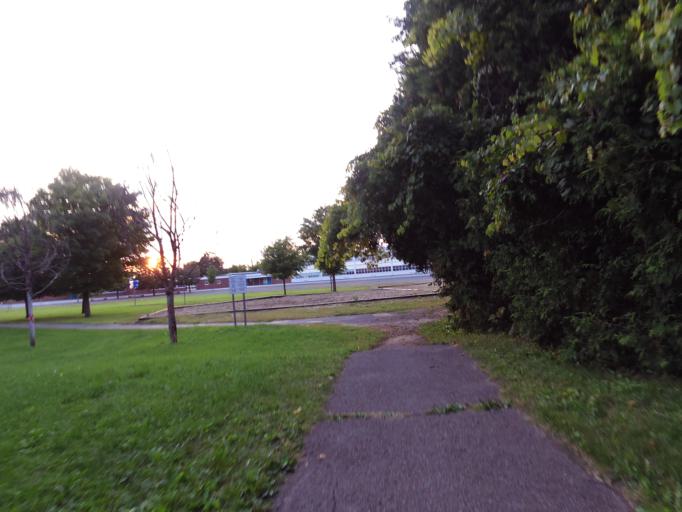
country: CA
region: Ontario
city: Bells Corners
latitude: 45.3240
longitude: -75.8238
